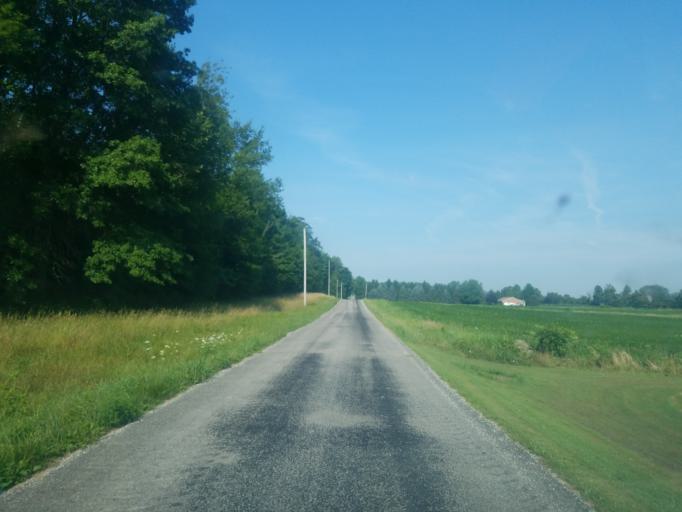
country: US
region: Ohio
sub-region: Huron County
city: Willard
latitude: 40.9674
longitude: -82.7994
